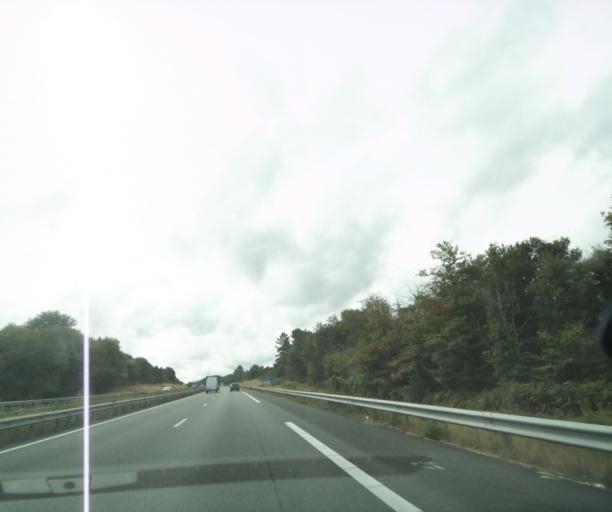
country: FR
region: Poitou-Charentes
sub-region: Departement de la Charente-Maritime
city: Saint-Genis-de-Saintonge
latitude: 45.4687
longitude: -0.6207
